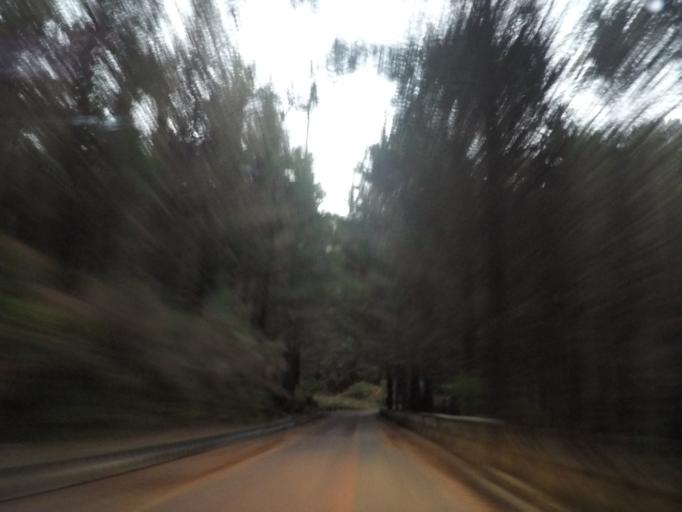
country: PT
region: Madeira
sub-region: Santa Cruz
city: Camacha
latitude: 32.7163
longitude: -16.8544
